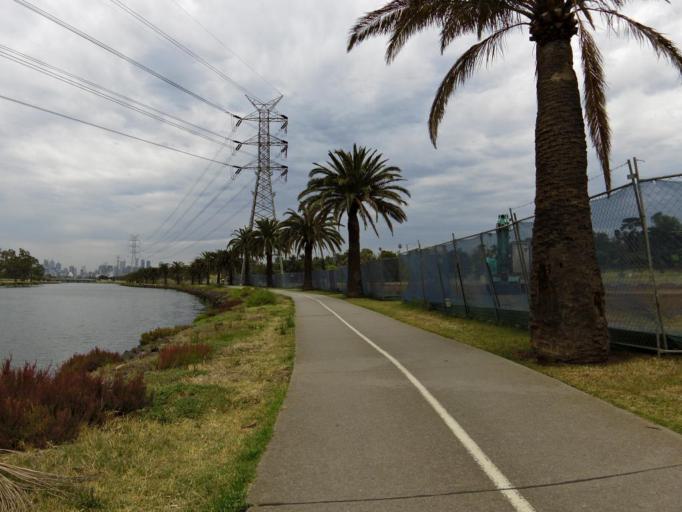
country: AU
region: Victoria
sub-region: Maribyrnong
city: Footscray
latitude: -37.7914
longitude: 144.9029
